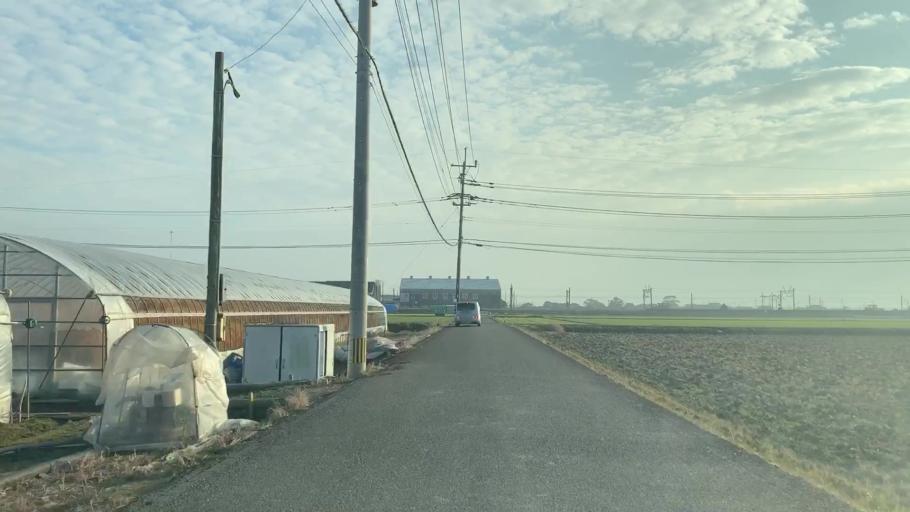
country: JP
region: Saga Prefecture
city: Saga-shi
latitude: 33.2613
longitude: 130.2603
